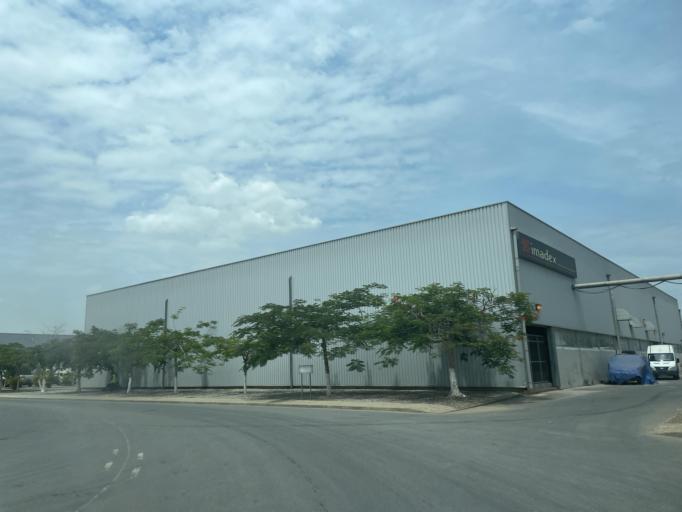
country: AO
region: Luanda
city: Luanda
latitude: -8.9616
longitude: 13.3898
